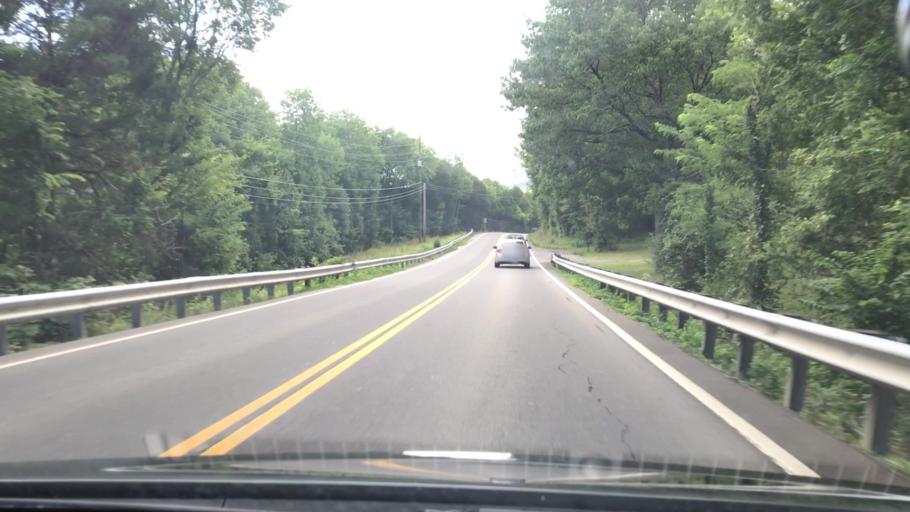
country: US
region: Tennessee
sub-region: Williamson County
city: Nolensville
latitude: 35.8516
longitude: -86.6027
